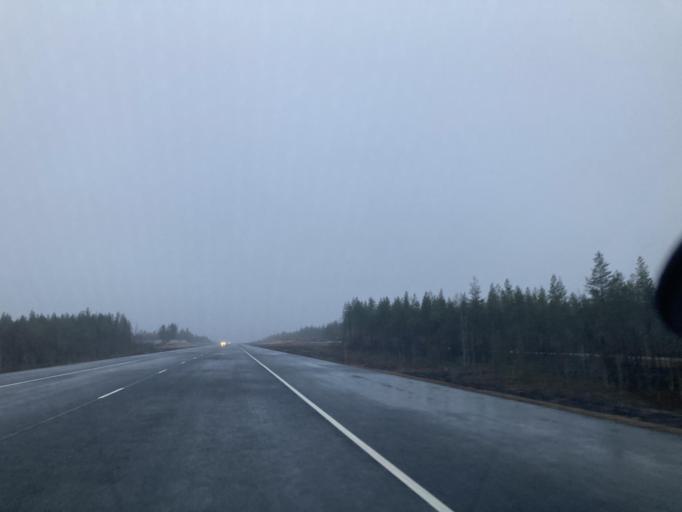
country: FI
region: Lapland
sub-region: Rovaniemi
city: Rovaniemi
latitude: 66.5832
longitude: 25.8006
